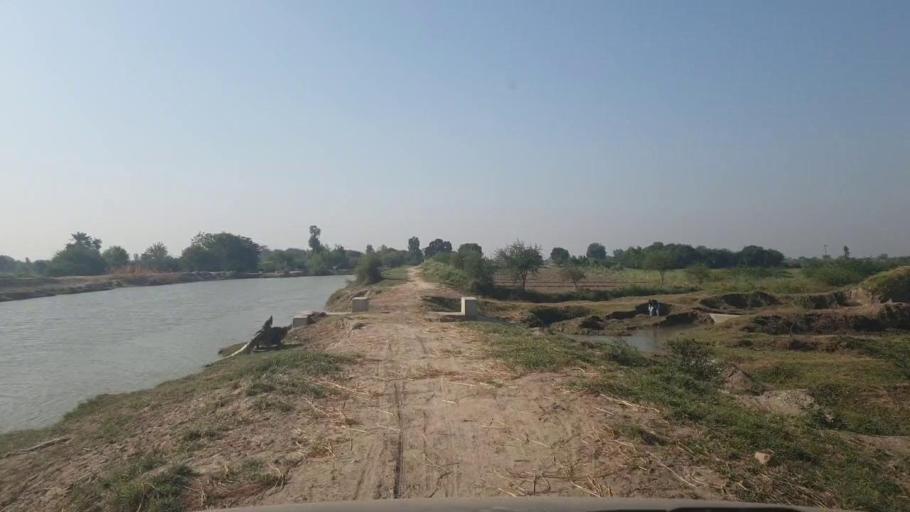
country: PK
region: Sindh
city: Badin
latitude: 24.6886
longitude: 68.8674
